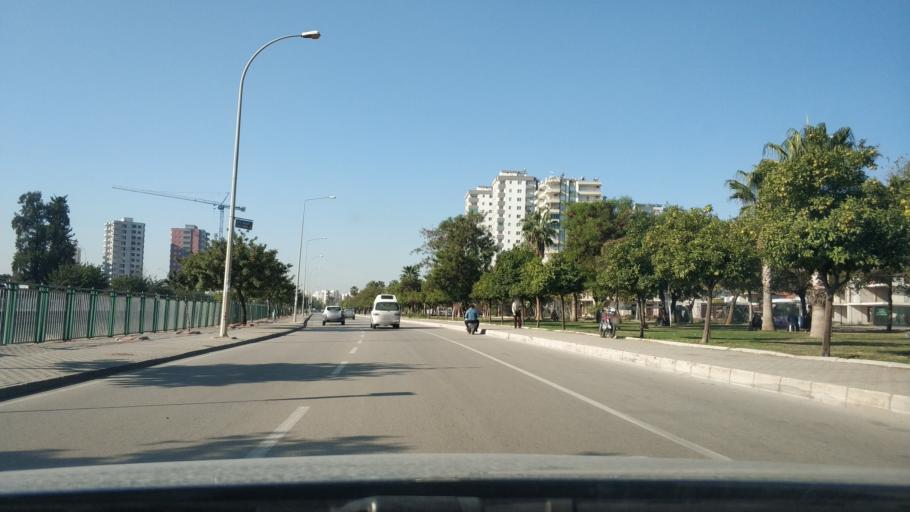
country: TR
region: Adana
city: Seyhan
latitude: 37.0113
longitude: 35.2938
